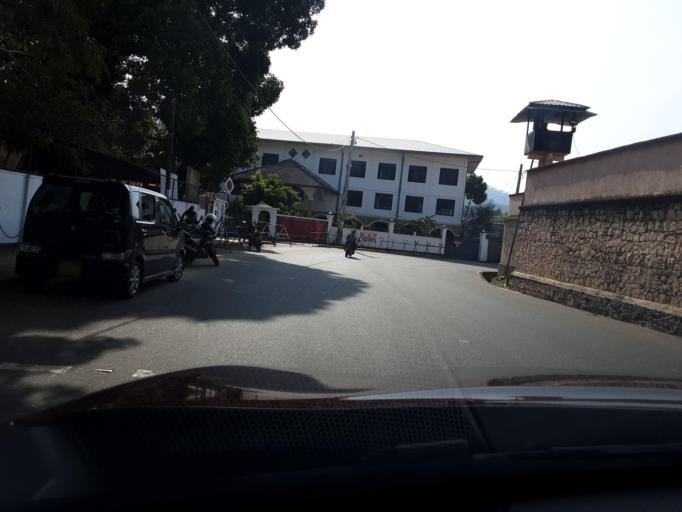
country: LK
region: Uva
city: Badulla
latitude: 6.9903
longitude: 81.0588
